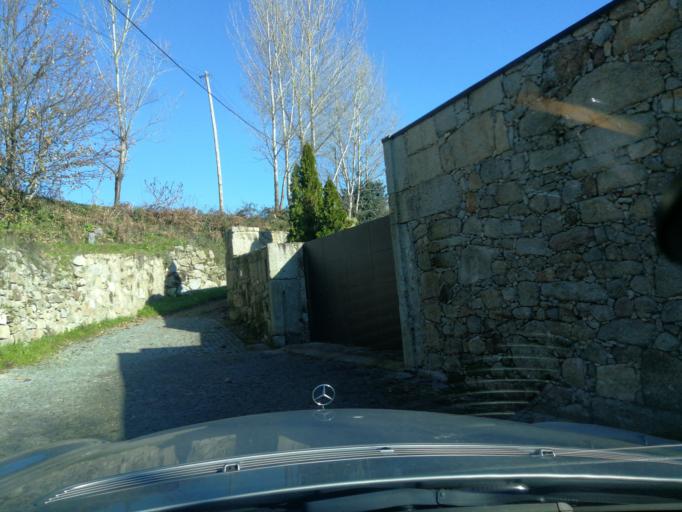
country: PT
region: Braga
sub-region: Braga
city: Adaufe
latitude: 41.6124
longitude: -8.3962
